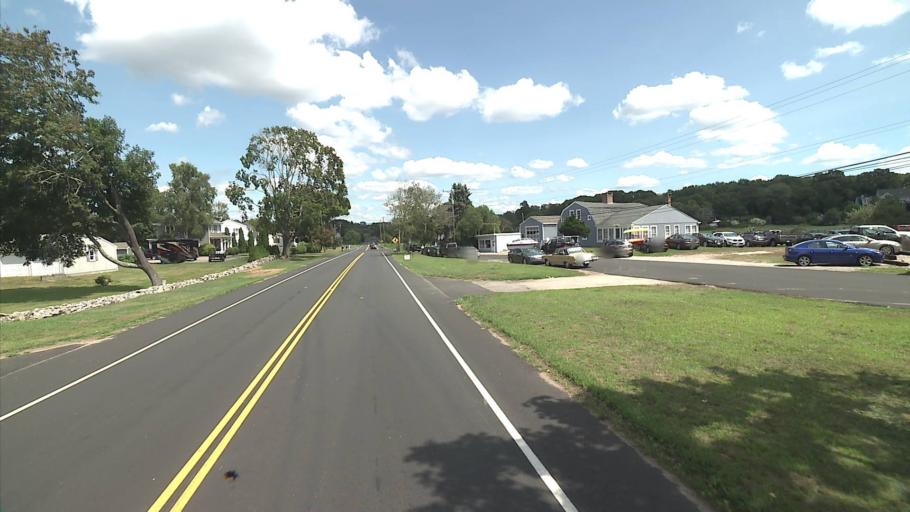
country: US
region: Connecticut
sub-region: New London County
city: Pawcatuck
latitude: 41.3577
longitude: -71.8811
